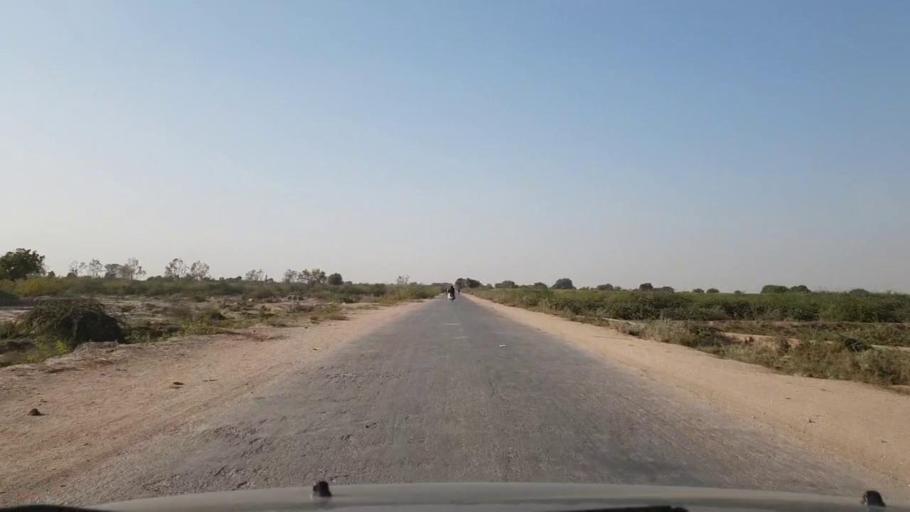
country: PK
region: Sindh
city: Tando Ghulam Ali
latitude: 25.1441
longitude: 68.8681
